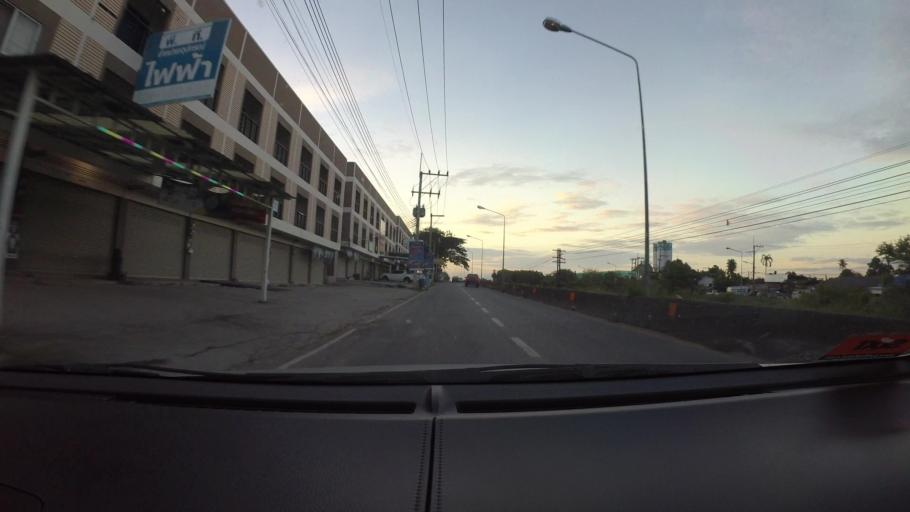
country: TH
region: Chon Buri
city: Phatthaya
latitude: 12.8600
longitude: 100.9135
